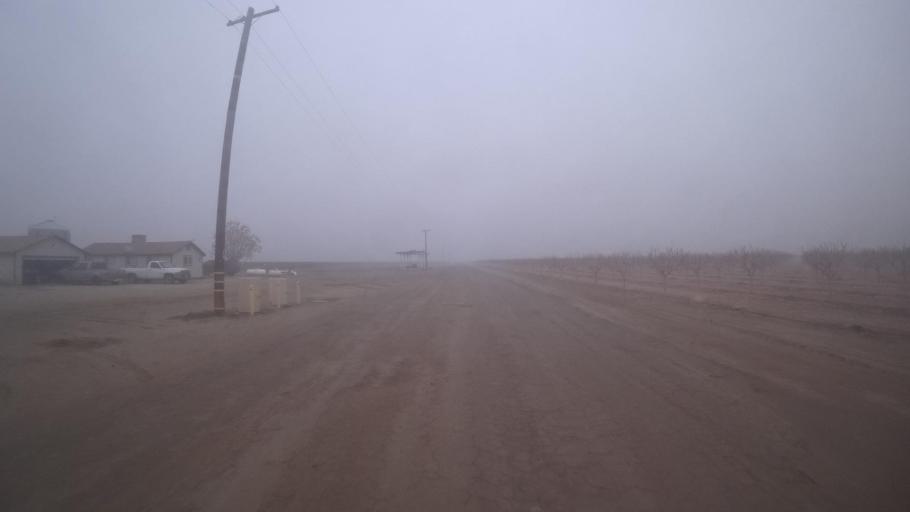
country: US
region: California
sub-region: Kern County
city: Buttonwillow
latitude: 35.4613
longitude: -119.5650
